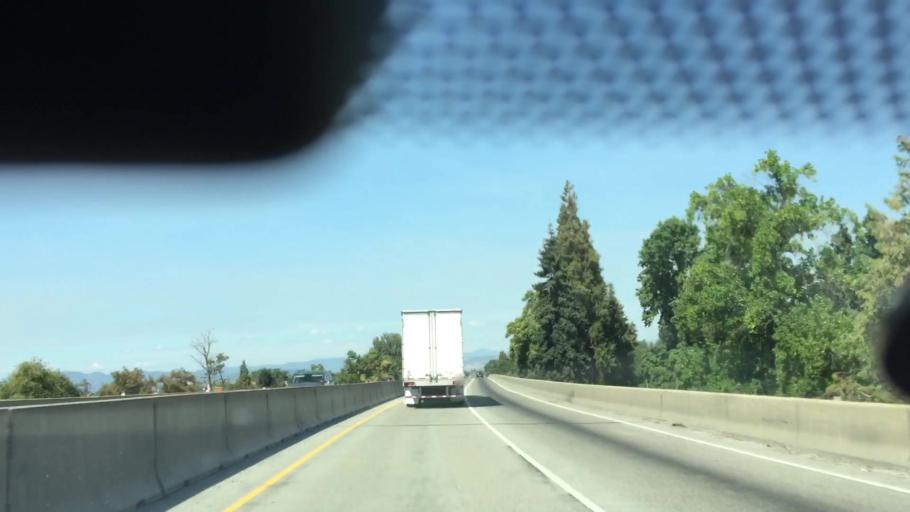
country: US
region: Oregon
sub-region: Jackson County
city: Medford
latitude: 42.3270
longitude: -122.8688
